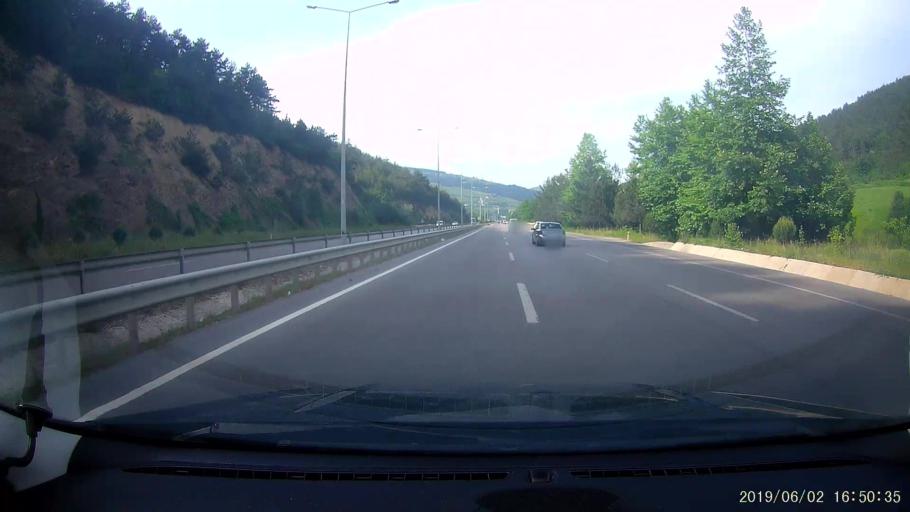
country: TR
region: Samsun
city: Taflan
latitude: 41.2577
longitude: 36.1740
